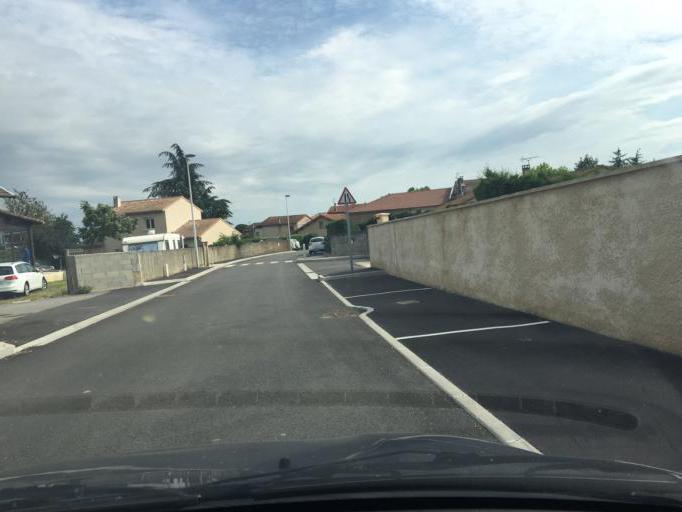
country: FR
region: Rhone-Alpes
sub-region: Departement de la Drome
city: Clerieux
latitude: 45.1080
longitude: 4.9276
